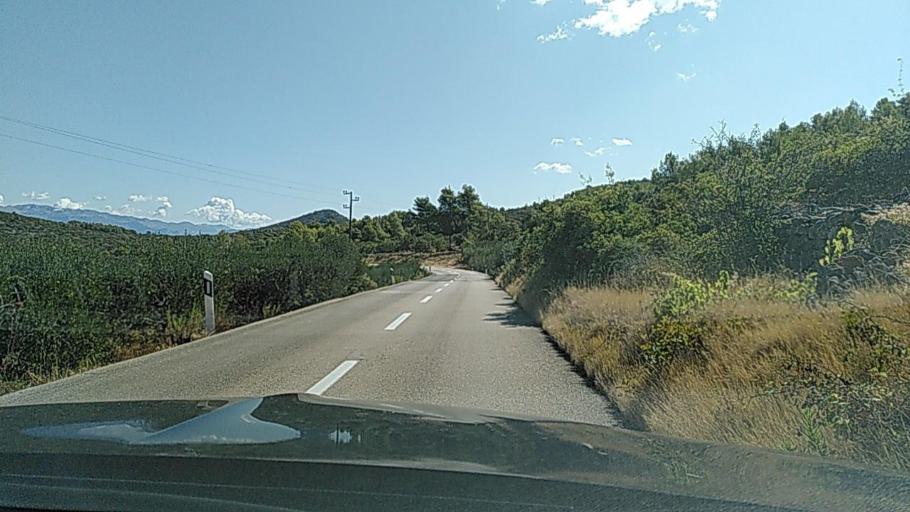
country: HR
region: Splitsko-Dalmatinska
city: Jelsa
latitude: 43.1433
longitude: 16.8209
